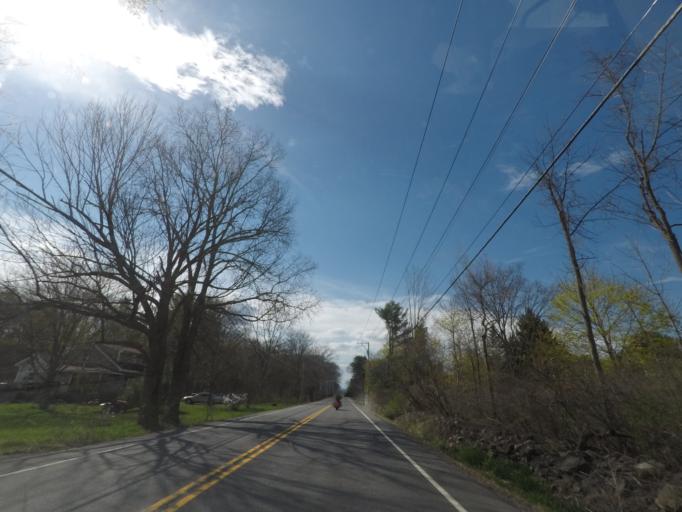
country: US
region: New York
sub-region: Greene County
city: Cairo
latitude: 42.3450
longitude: -74.0347
